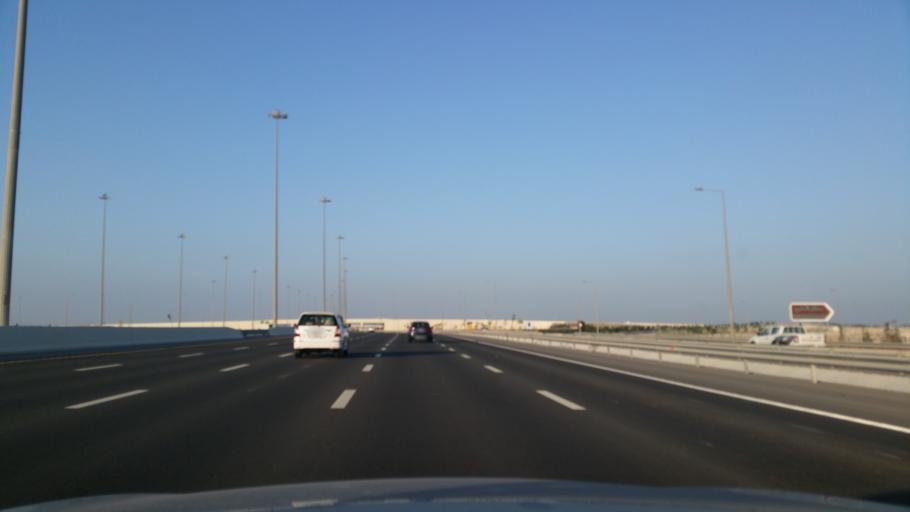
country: QA
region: Al Khawr
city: Al Khawr
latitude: 25.6345
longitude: 51.4905
